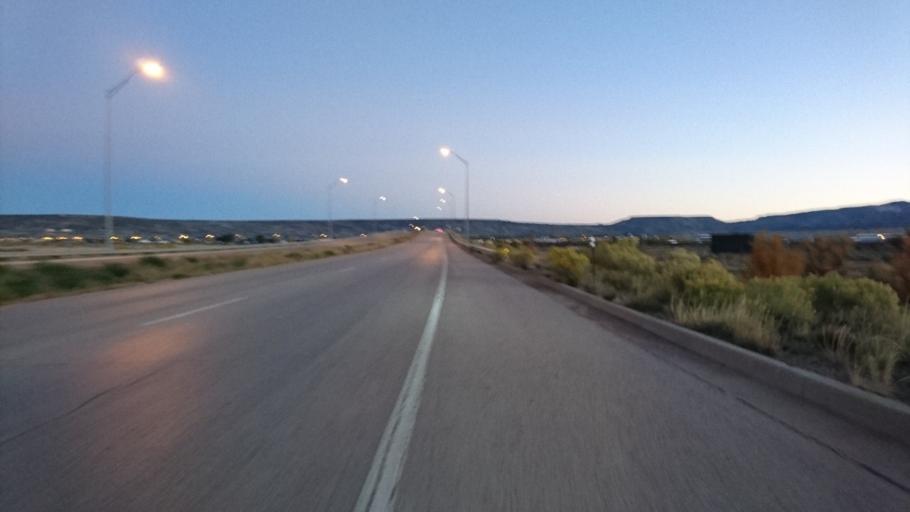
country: US
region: New Mexico
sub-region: Cibola County
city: Grants
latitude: 35.1336
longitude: -107.8274
